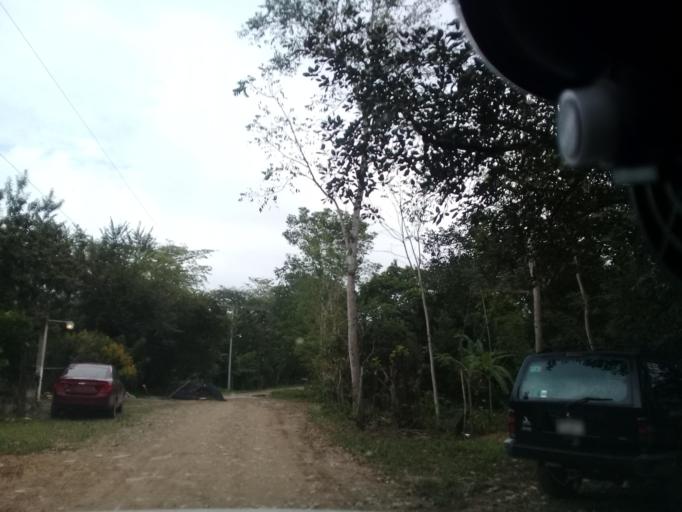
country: MX
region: Hidalgo
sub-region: Huejutla de Reyes
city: Chalahuiyapa
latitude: 21.1637
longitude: -98.3498
